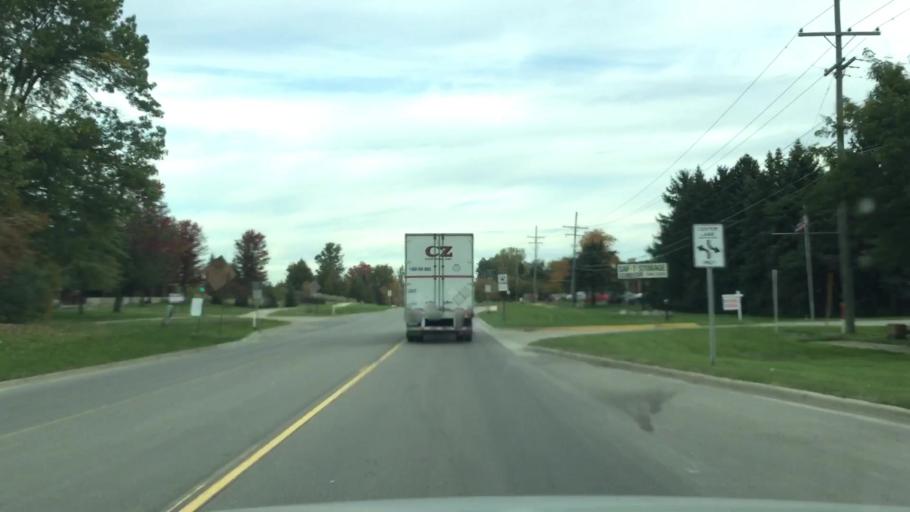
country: US
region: Michigan
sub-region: Oakland County
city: Wixom
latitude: 42.5100
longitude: -83.5166
